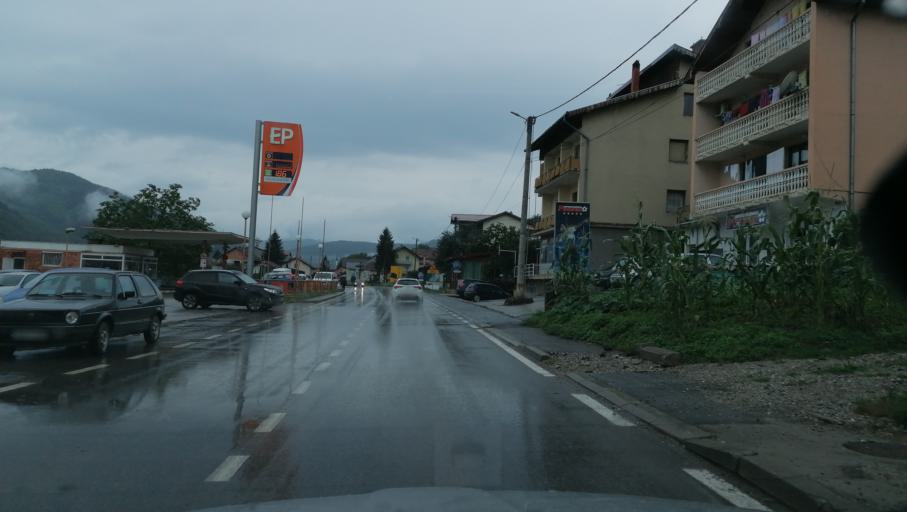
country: BA
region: Federation of Bosnia and Herzegovina
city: Gorazde
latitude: 43.6737
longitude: 18.9832
